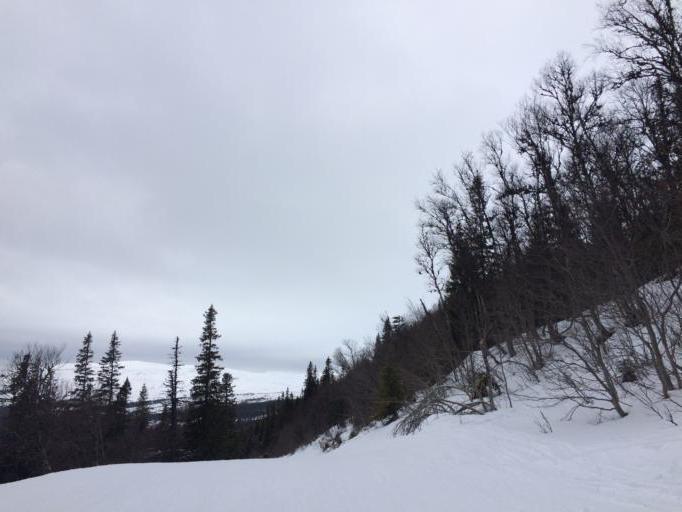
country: SE
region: Jaemtland
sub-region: Are Kommun
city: Are
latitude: 63.4096
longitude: 13.0722
